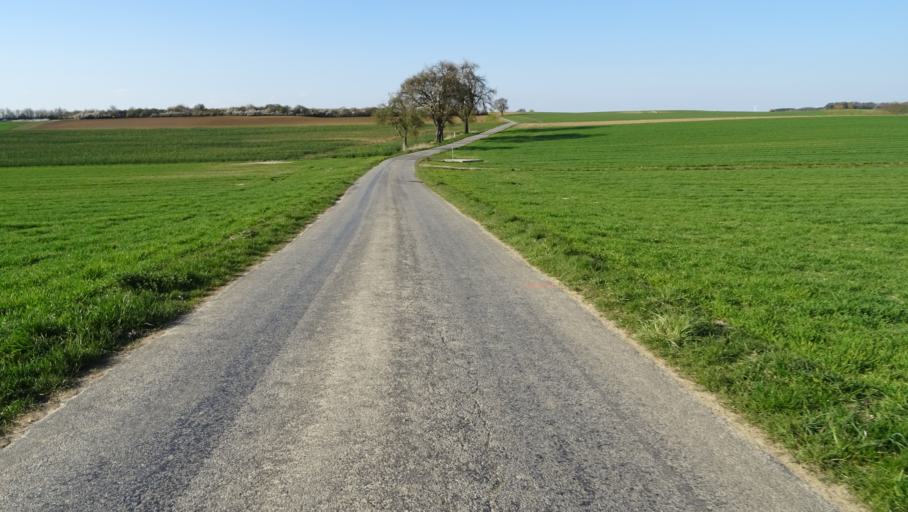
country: DE
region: Baden-Wuerttemberg
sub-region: Karlsruhe Region
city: Billigheim
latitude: 49.3820
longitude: 9.2344
